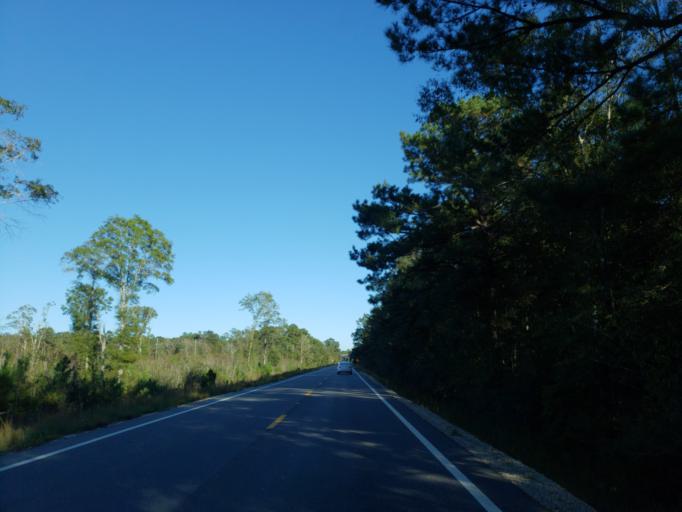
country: US
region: Mississippi
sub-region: Perry County
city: Richton
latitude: 31.3586
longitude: -89.0315
